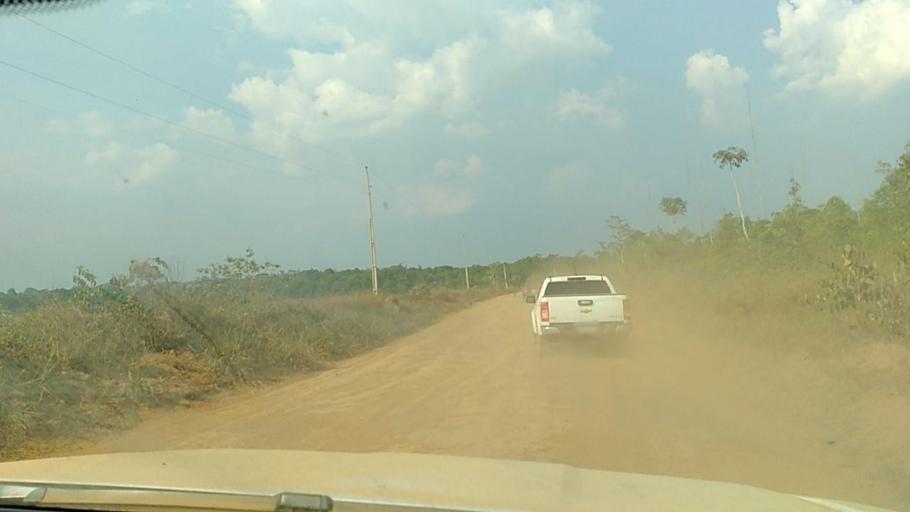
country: BR
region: Rondonia
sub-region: Porto Velho
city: Porto Velho
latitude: -8.6728
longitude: -64.0157
